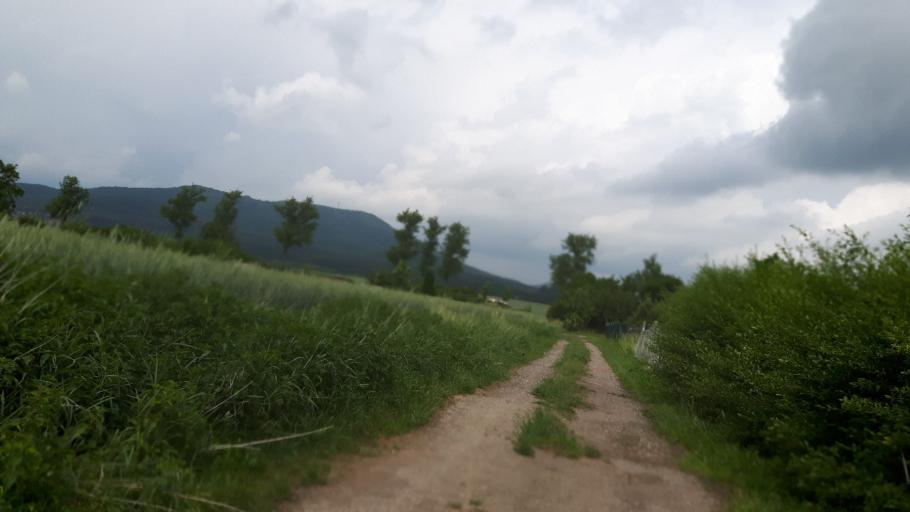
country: DE
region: Thuringia
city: Gleichamberg
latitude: 50.3636
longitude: 10.6309
